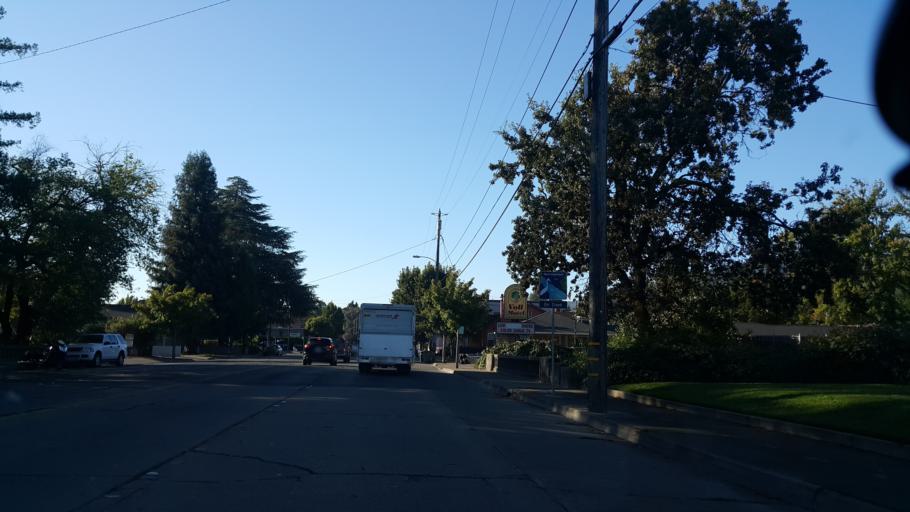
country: US
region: California
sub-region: Mendocino County
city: Ukiah
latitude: 39.1562
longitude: -123.2084
